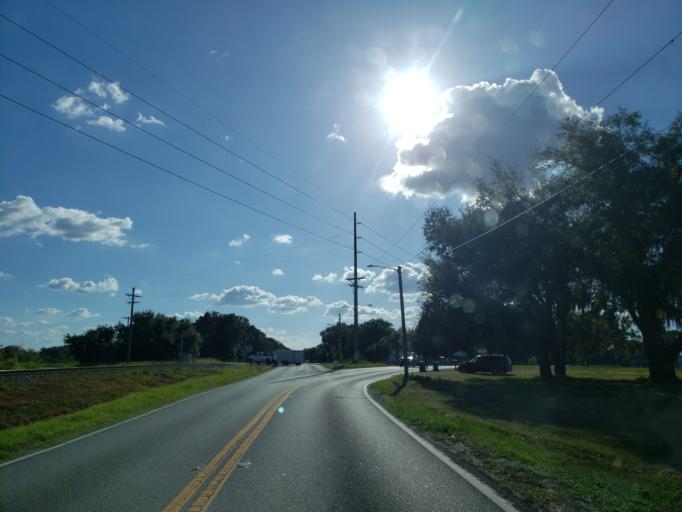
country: US
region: Florida
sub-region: Hillsborough County
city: Dover
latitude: 27.9673
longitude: -82.2024
